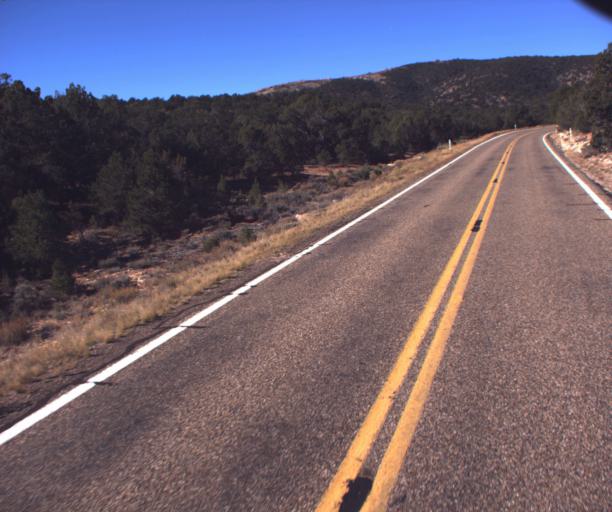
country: US
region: Arizona
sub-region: Coconino County
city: Fredonia
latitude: 36.7397
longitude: -112.1042
